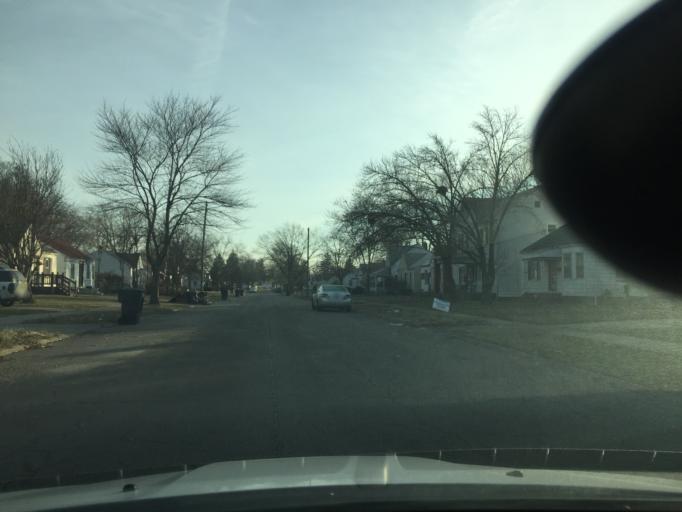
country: US
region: Michigan
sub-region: Macomb County
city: Eastpointe
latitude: 42.4402
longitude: -82.9530
